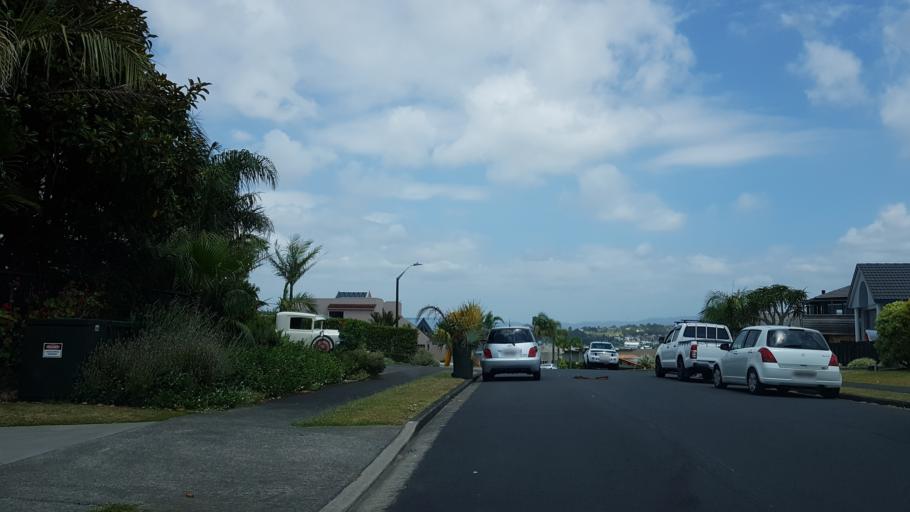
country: NZ
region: Auckland
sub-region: Auckland
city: Rosebank
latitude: -36.7995
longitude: 174.6498
